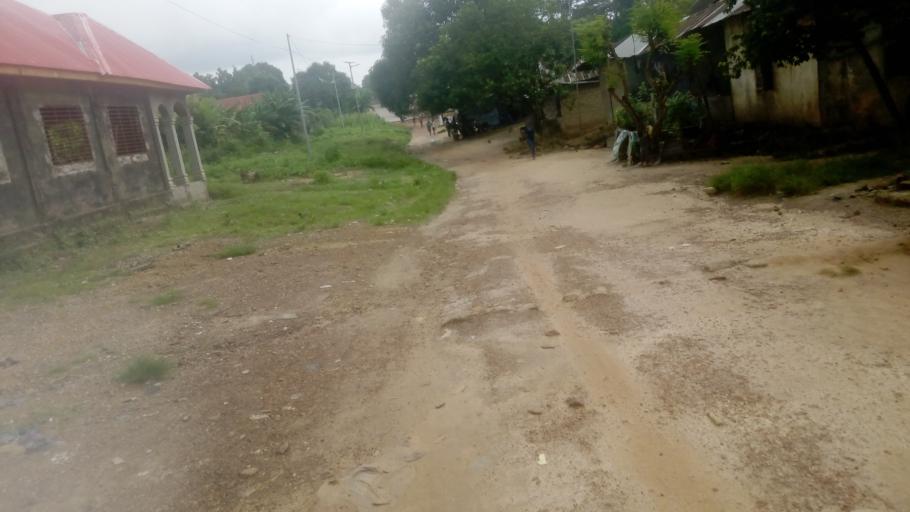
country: SL
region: Northern Province
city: Lunsar
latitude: 8.6820
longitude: -12.5356
